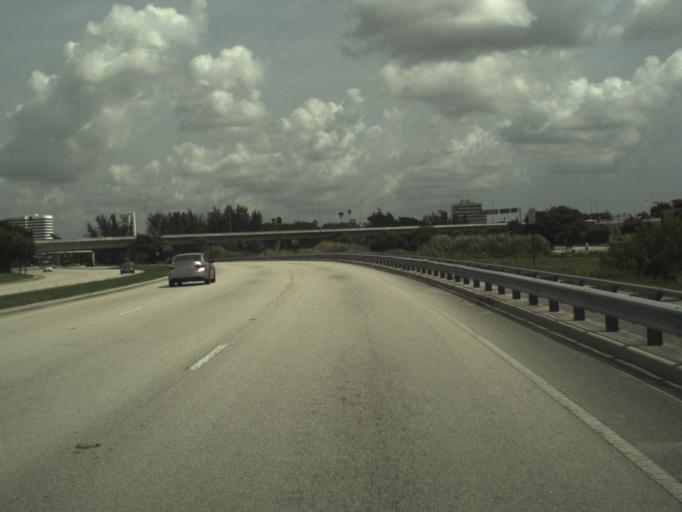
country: US
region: Florida
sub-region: Palm Beach County
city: West Palm Beach
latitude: 26.6840
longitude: -80.0735
